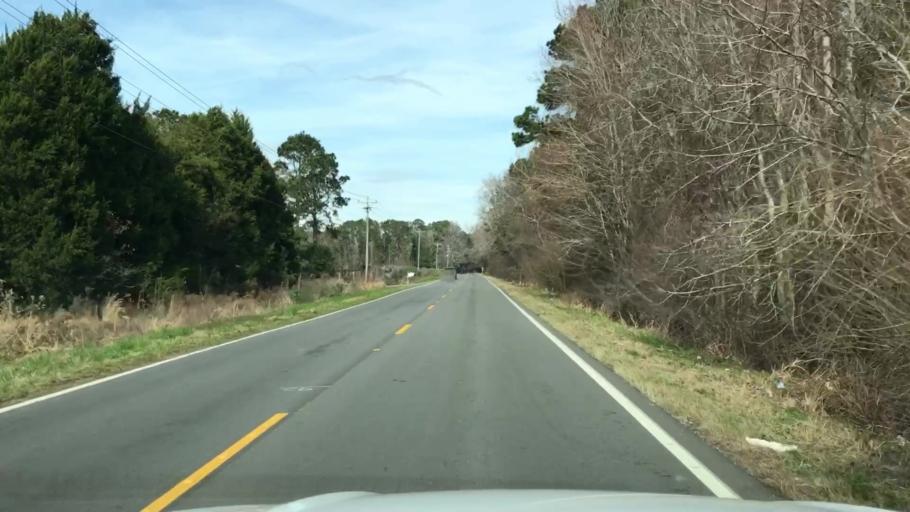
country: US
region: South Carolina
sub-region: Charleston County
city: Folly Beach
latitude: 32.7214
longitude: -80.0224
